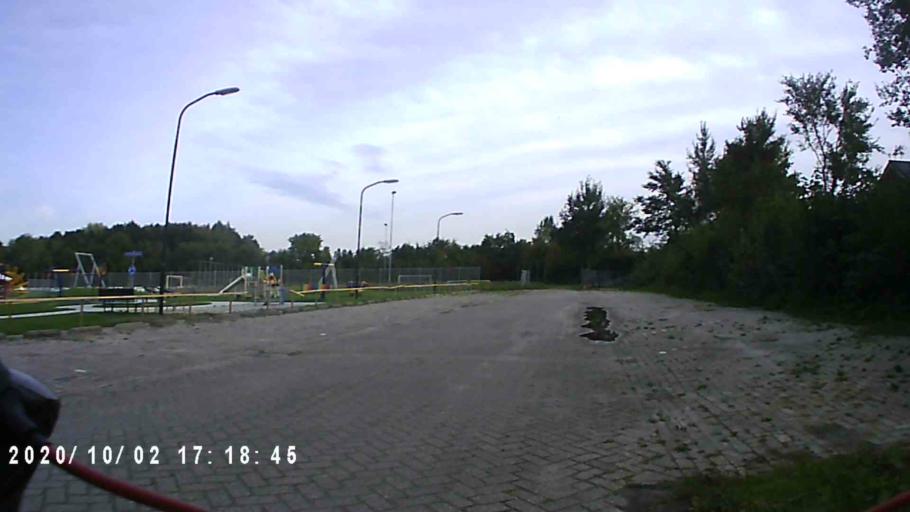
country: NL
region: Groningen
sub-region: Gemeente De Marne
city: Ulrum
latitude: 53.3403
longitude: 6.3064
